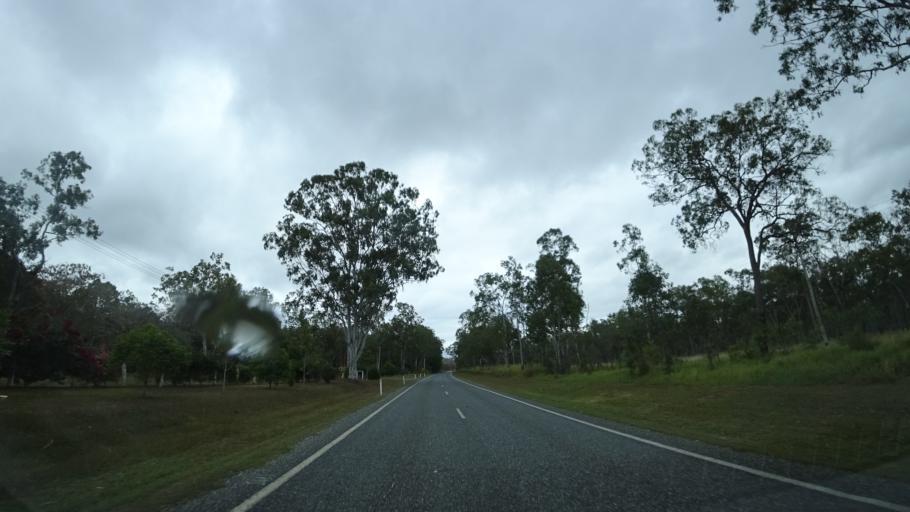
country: AU
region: Queensland
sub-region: Cairns
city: Port Douglas
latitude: -16.7311
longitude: 145.3520
